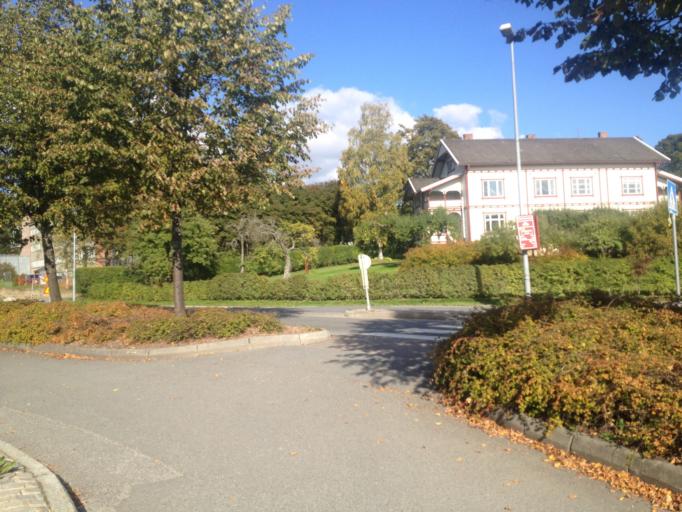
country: NO
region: Akershus
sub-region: As
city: As
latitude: 59.6650
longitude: 10.7723
